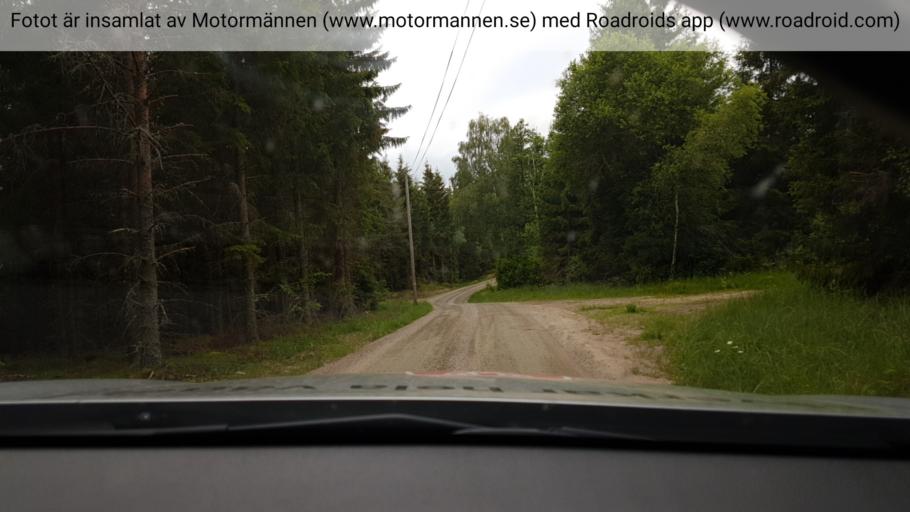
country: SE
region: Joenkoeping
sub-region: Mullsjo Kommun
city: Mullsjoe
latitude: 57.9171
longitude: 13.7022
